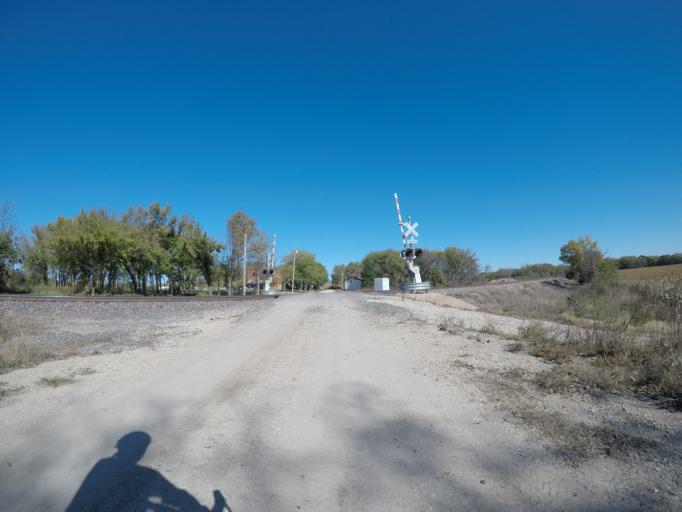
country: US
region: Kansas
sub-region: Wabaunsee County
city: Alma
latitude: 38.9436
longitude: -96.4042
